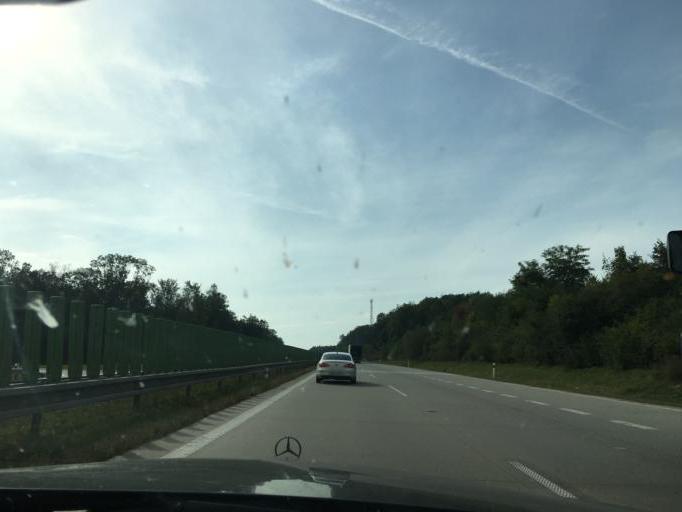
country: CZ
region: Pardubicky
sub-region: Okres Pardubice
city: Lazne Bohdanec
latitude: 50.1381
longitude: 15.6350
